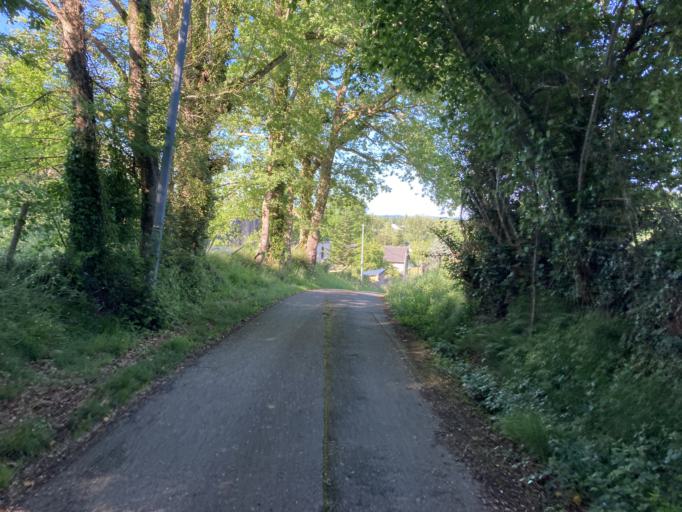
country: FR
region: Aquitaine
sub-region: Departement des Pyrenees-Atlantiques
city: Artiguelouve
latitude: 43.3118
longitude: -0.4797
